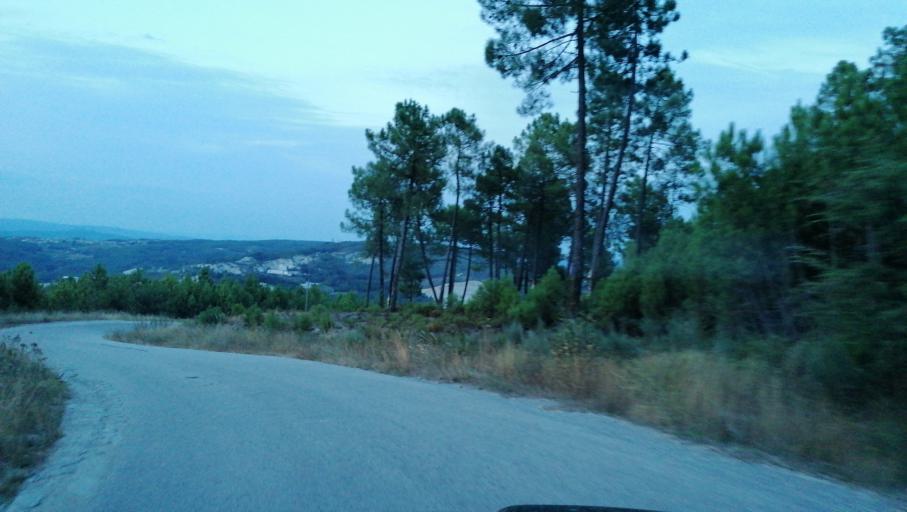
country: PT
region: Vila Real
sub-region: Vila Pouca de Aguiar
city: Vila Pouca de Aguiar
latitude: 41.5554
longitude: -7.6290
